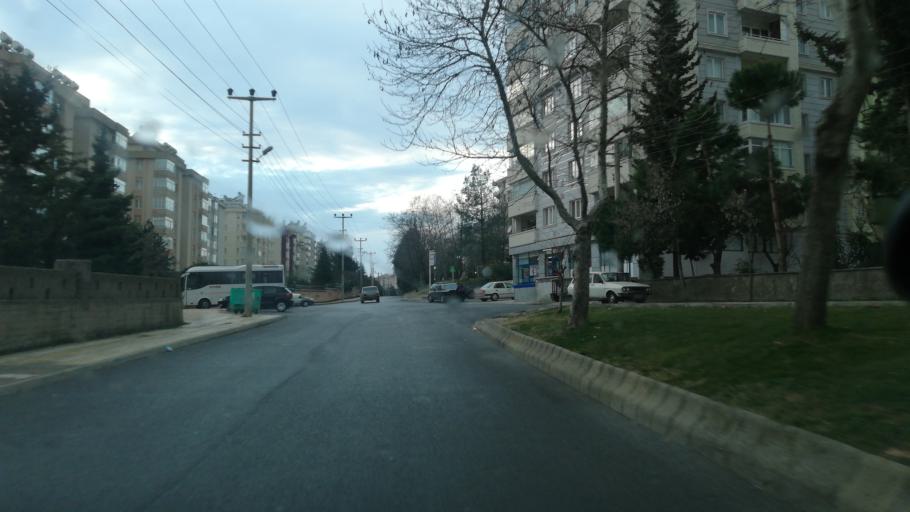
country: TR
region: Kahramanmaras
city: Kahramanmaras
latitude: 37.5881
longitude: 36.8944
